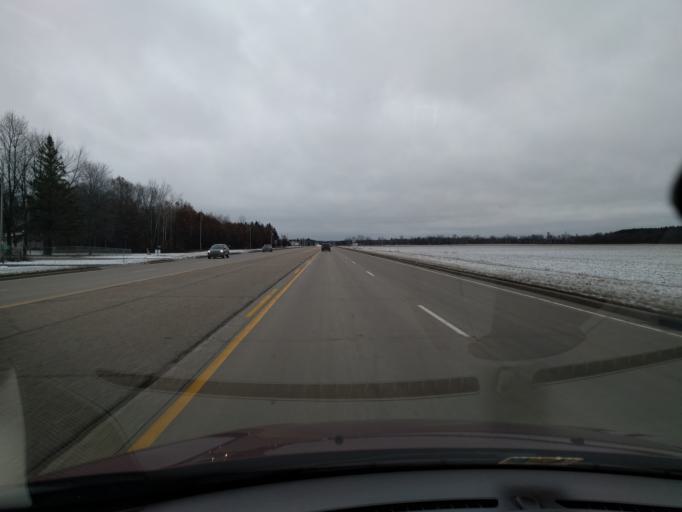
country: US
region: Wisconsin
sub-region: Portage County
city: Whiting
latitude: 44.5234
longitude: -89.4868
